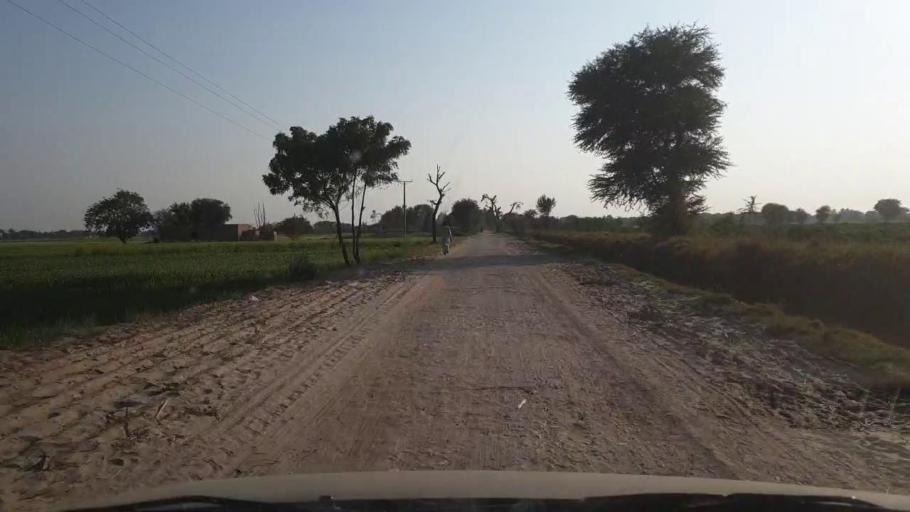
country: PK
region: Sindh
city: Samaro
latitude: 25.2834
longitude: 69.3613
